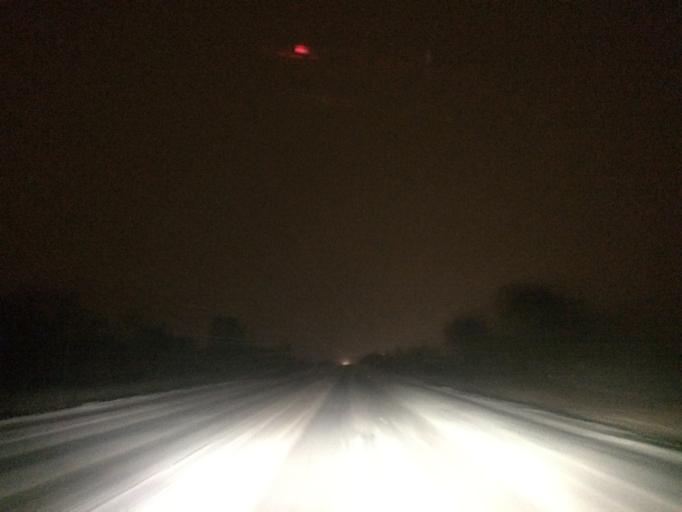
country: RU
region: Tula
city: Kosaya Gora
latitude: 54.1559
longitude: 37.4492
